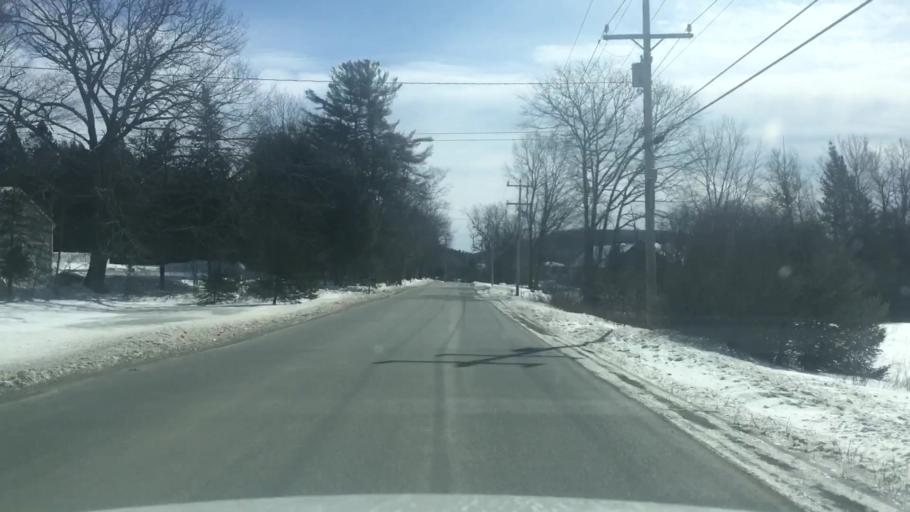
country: US
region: Maine
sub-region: Penobscot County
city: Holden
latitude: 44.7433
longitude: -68.6300
